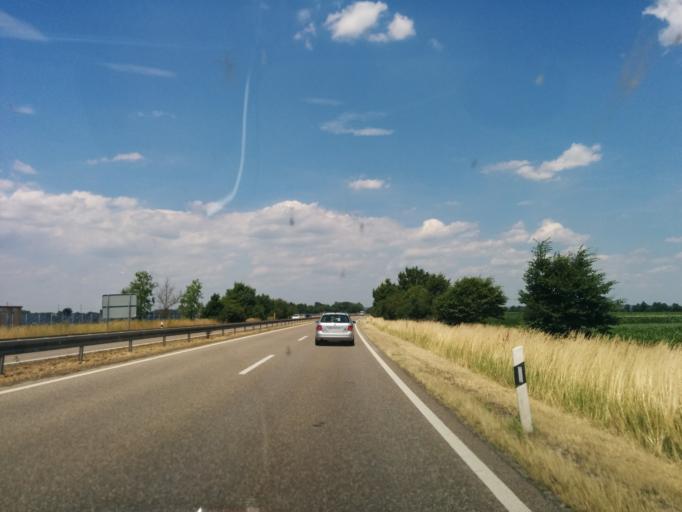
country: DE
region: Bavaria
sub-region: Swabia
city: Nordendorf
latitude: 48.6063
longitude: 10.8382
